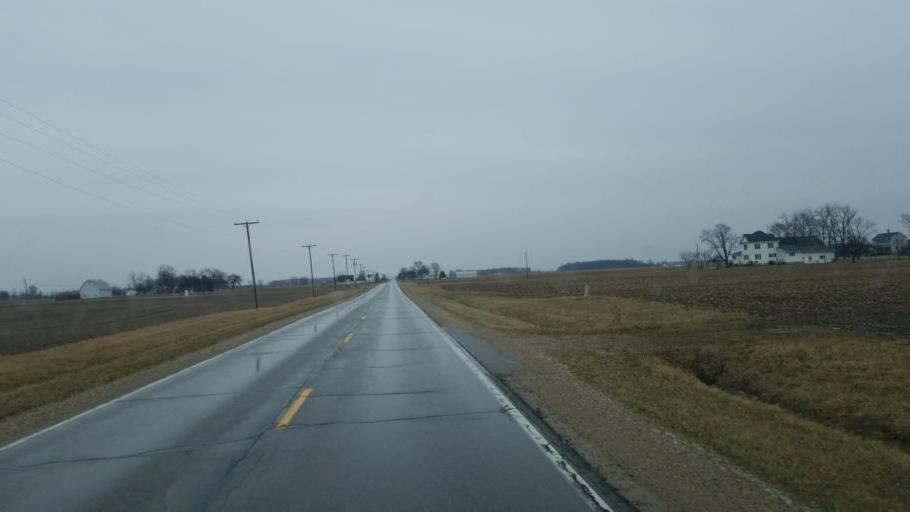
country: US
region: Indiana
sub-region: Adams County
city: Geneva
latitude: 40.6289
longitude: -85.0412
